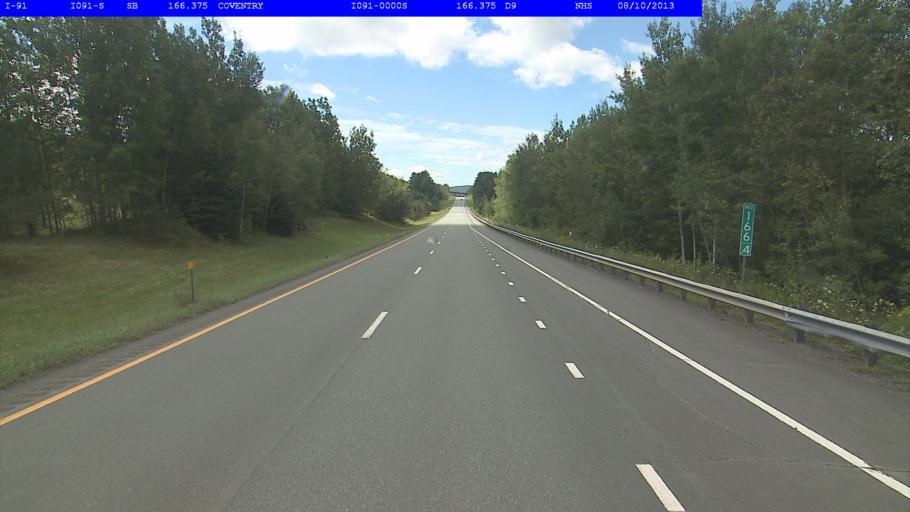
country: US
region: Vermont
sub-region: Orleans County
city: Newport
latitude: 44.8716
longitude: -72.1785
